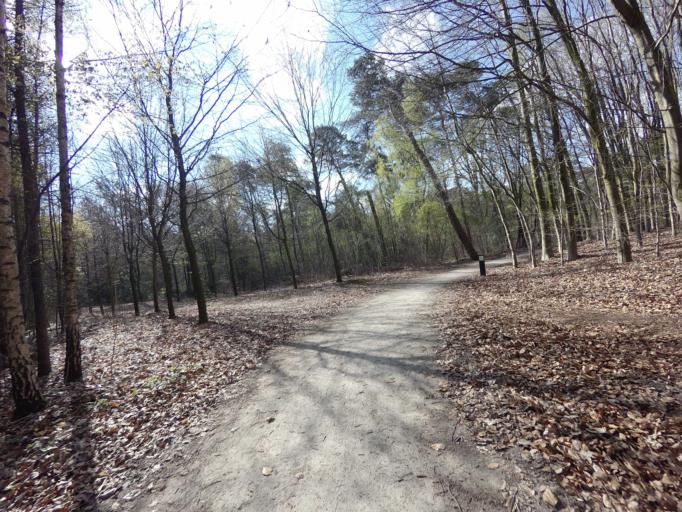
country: NL
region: Gelderland
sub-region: Gemeente Ede
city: Lunteren
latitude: 52.0821
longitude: 5.6499
